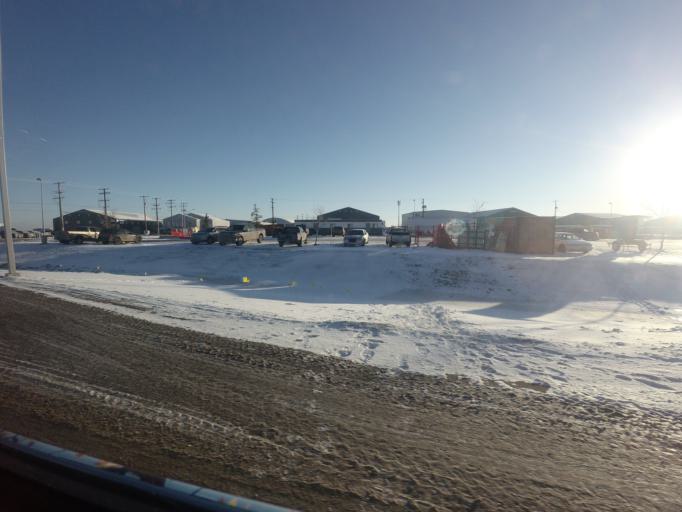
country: CA
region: Saskatchewan
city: Saskatoon
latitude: 52.1690
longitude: -106.6869
